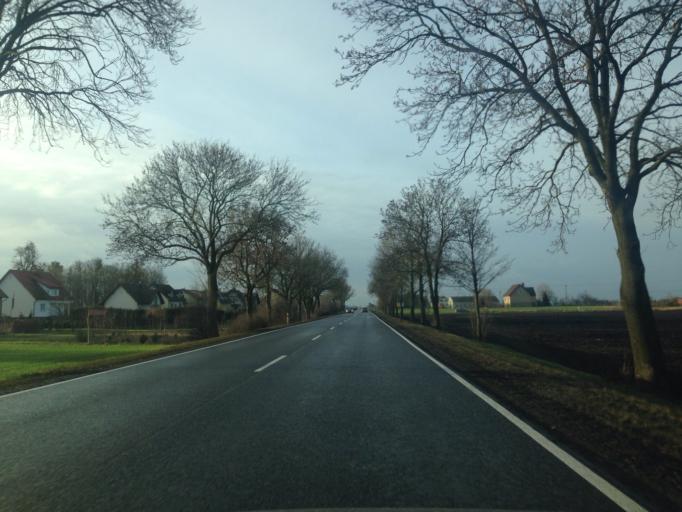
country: PL
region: Kujawsko-Pomorskie
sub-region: Powiat torunski
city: Lubicz Gorny
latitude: 53.1008
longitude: 18.7860
